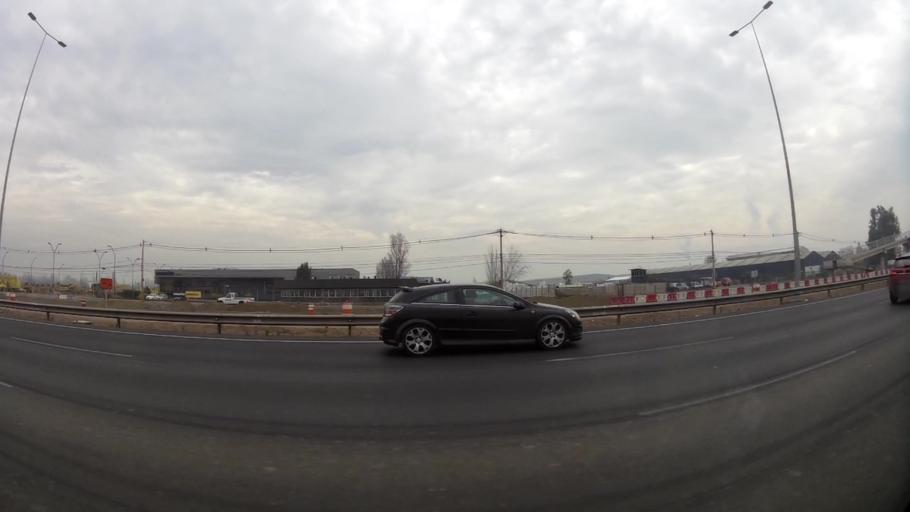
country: CL
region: Santiago Metropolitan
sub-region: Provincia de Chacabuco
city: Chicureo Abajo
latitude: -33.2639
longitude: -70.7460
